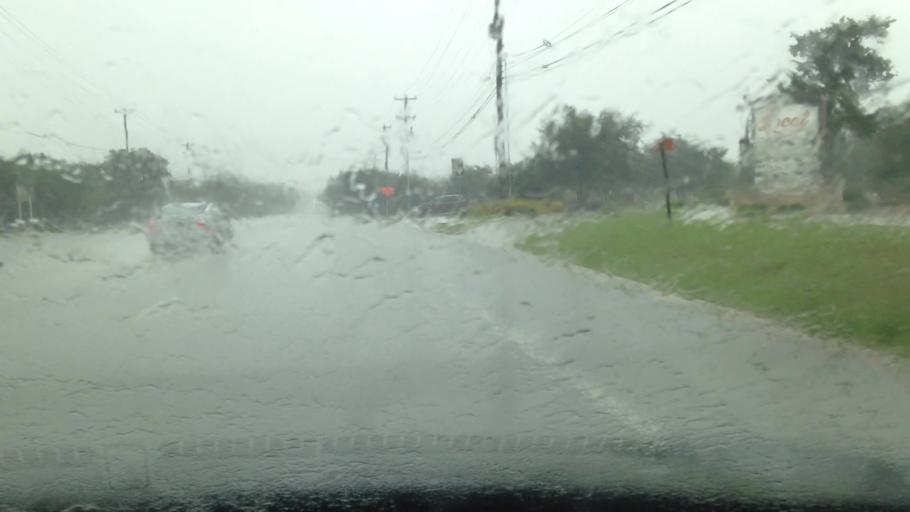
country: US
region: Texas
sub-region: Bexar County
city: Shavano Park
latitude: 29.5982
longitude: -98.5632
